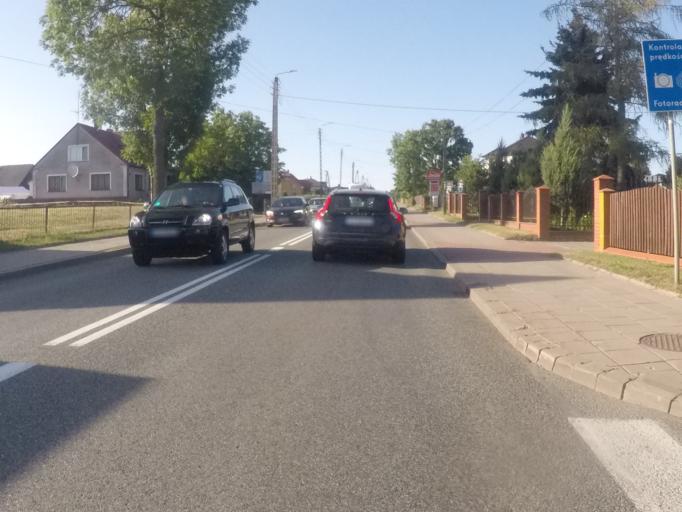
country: PL
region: Podlasie
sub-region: Powiat sokolski
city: Suchowola
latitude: 53.5725
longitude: 23.1046
